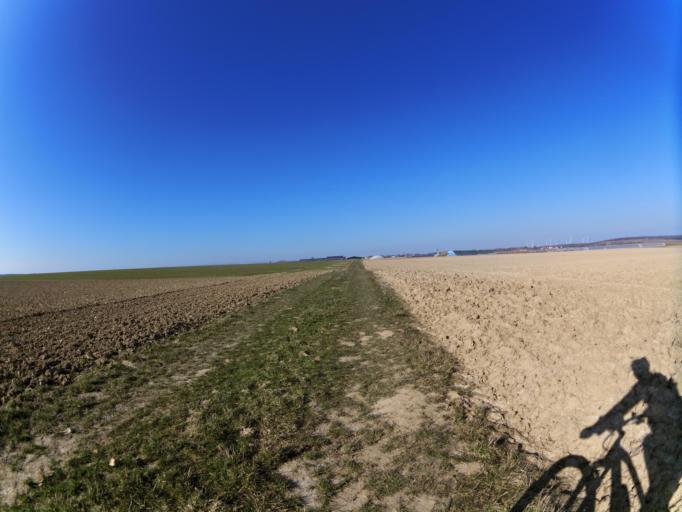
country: DE
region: Bavaria
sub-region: Regierungsbezirk Unterfranken
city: Bergtheim
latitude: 49.8820
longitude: 10.0624
